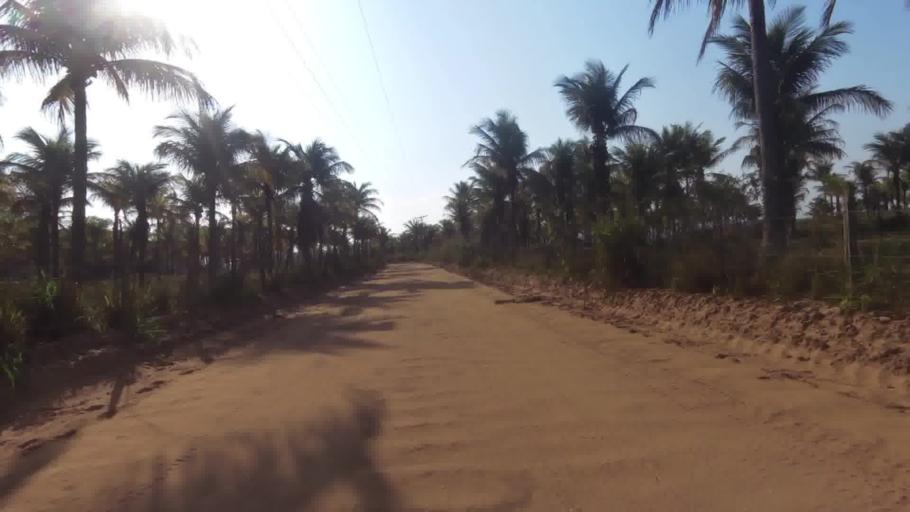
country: BR
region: Espirito Santo
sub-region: Piuma
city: Piuma
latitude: -20.8496
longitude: -40.7644
